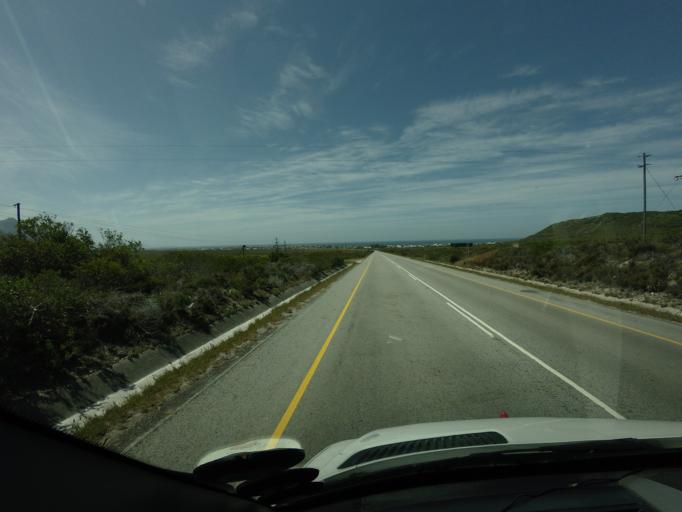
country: ZA
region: Western Cape
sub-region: Overberg District Municipality
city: Grabouw
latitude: -34.3544
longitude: 18.8593
